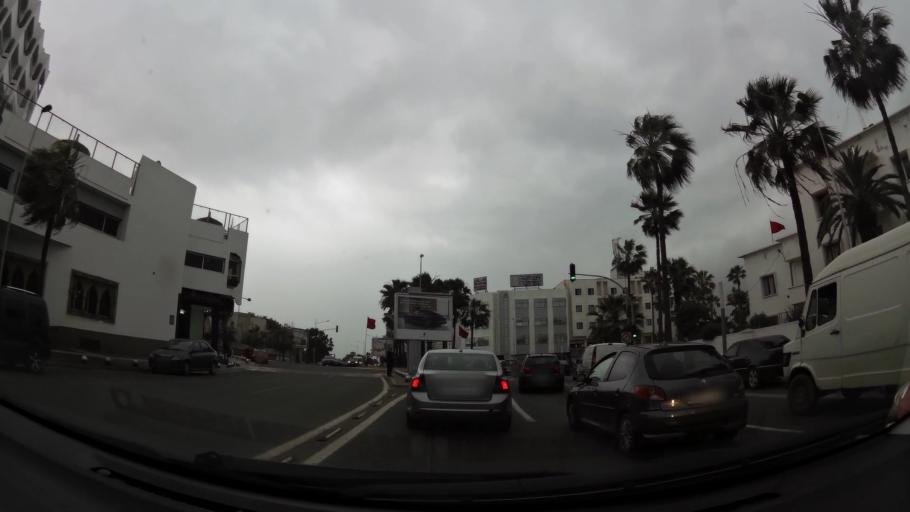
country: MA
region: Grand Casablanca
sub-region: Casablanca
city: Casablanca
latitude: 33.5918
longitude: -7.6769
